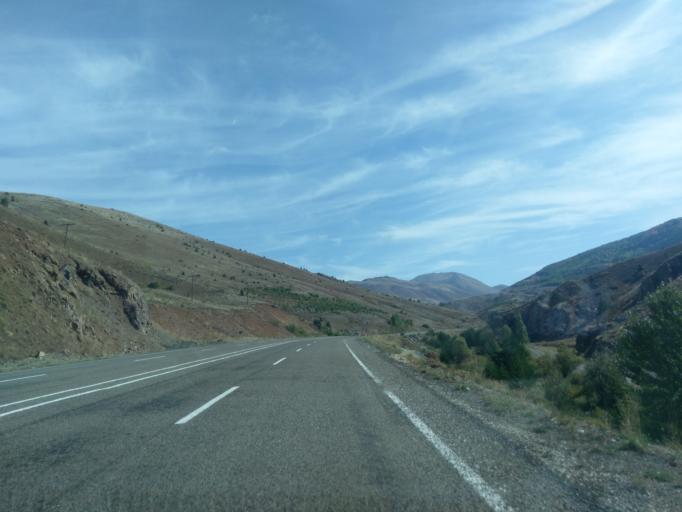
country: TR
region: Sivas
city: Imranli
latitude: 39.8540
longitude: 38.2992
